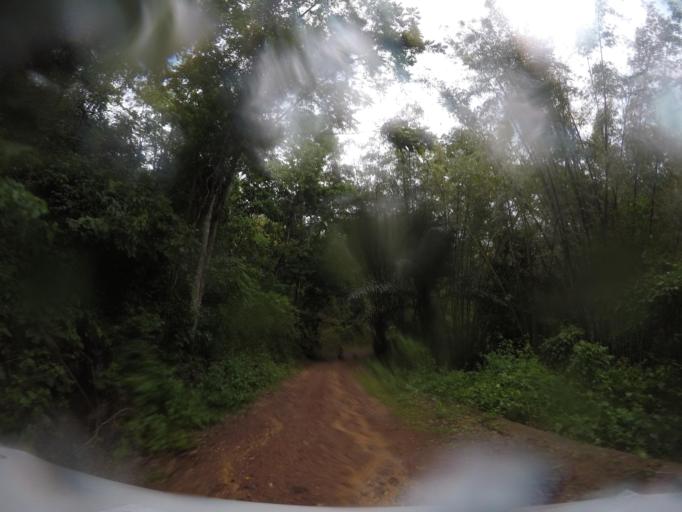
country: TL
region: Baucau
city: Venilale
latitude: -8.6294
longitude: 126.4325
